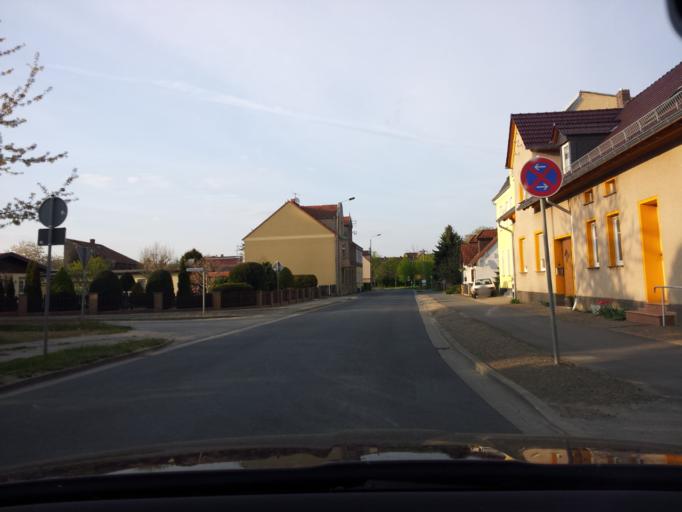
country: DE
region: Brandenburg
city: Dahme
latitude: 51.8662
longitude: 13.4193
